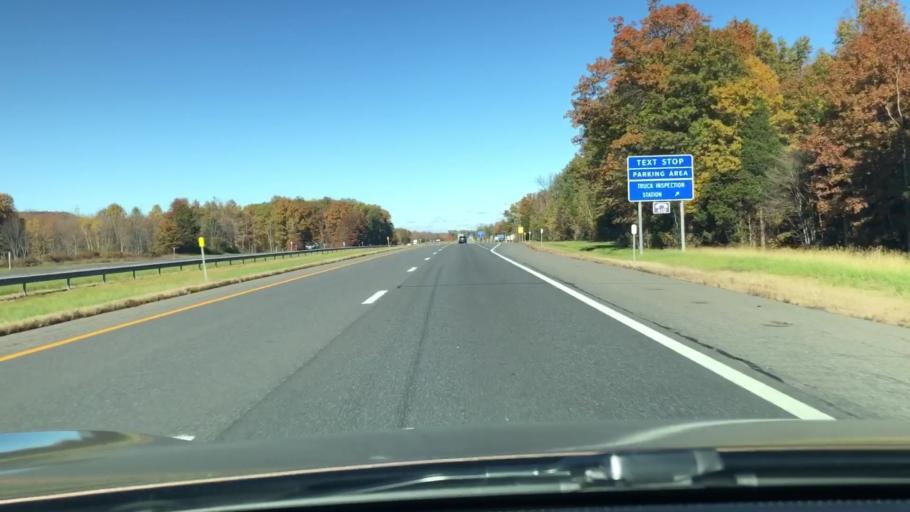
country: US
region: New York
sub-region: Ulster County
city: Saugerties South
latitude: 42.0499
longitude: -73.9854
